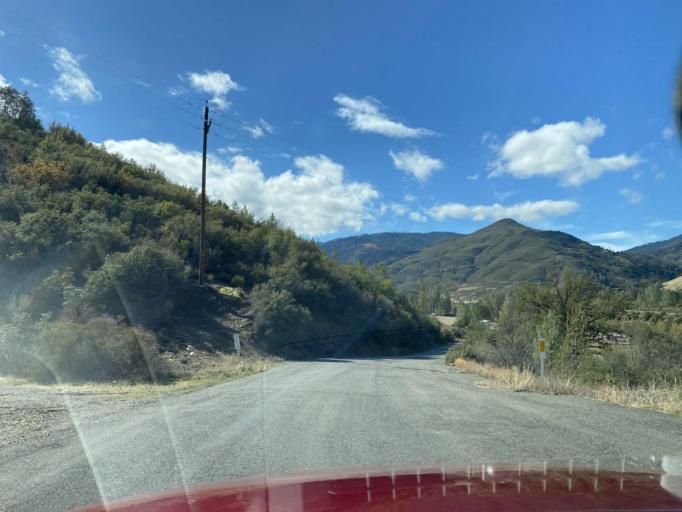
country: US
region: California
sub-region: Lake County
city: Lucerne
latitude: 39.3567
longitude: -122.6521
